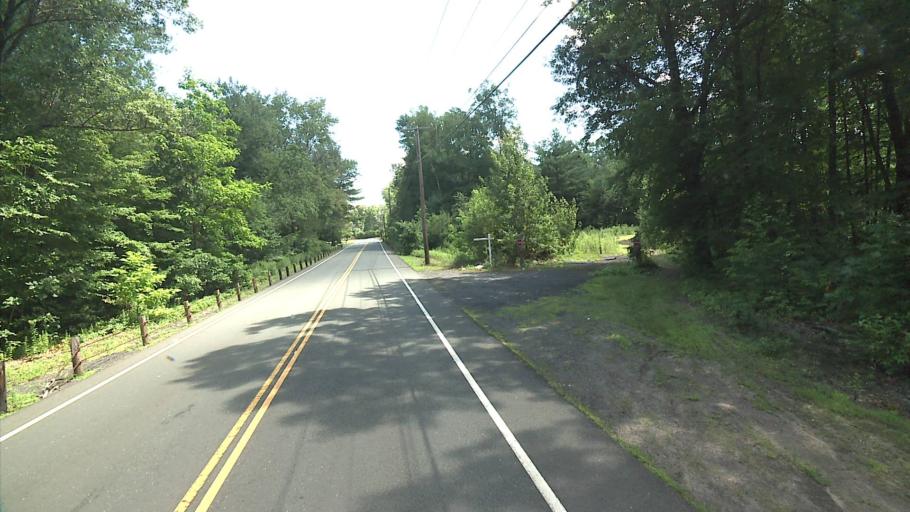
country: US
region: Massachusetts
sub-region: Hampden County
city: Southwick
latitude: 42.0206
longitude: -72.7519
